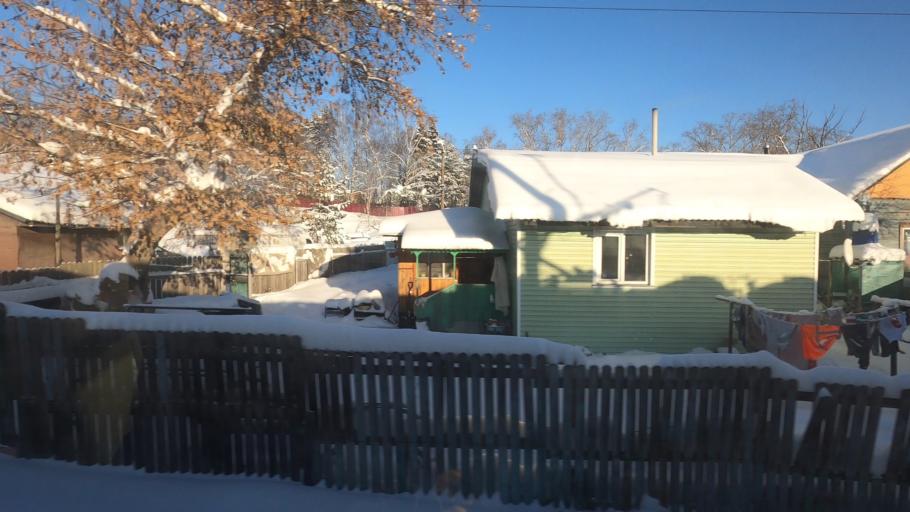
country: RU
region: Moskovskaya
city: Dmitrov
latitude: 56.3920
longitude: 37.5040
